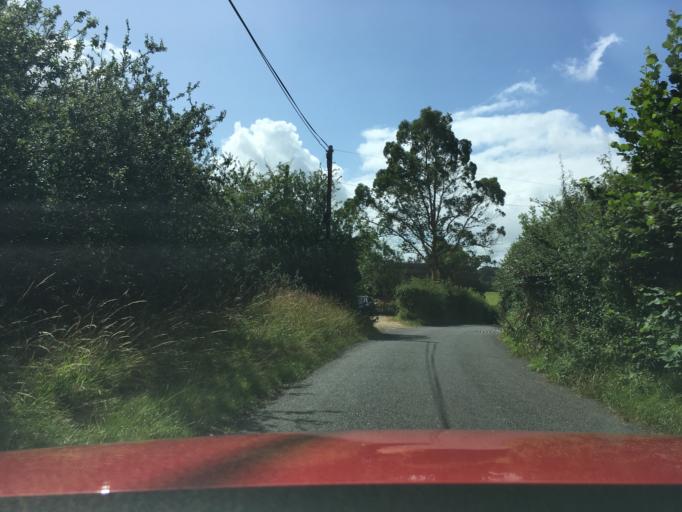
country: GB
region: England
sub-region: West Berkshire
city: Wickham
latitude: 51.4276
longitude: -1.4128
